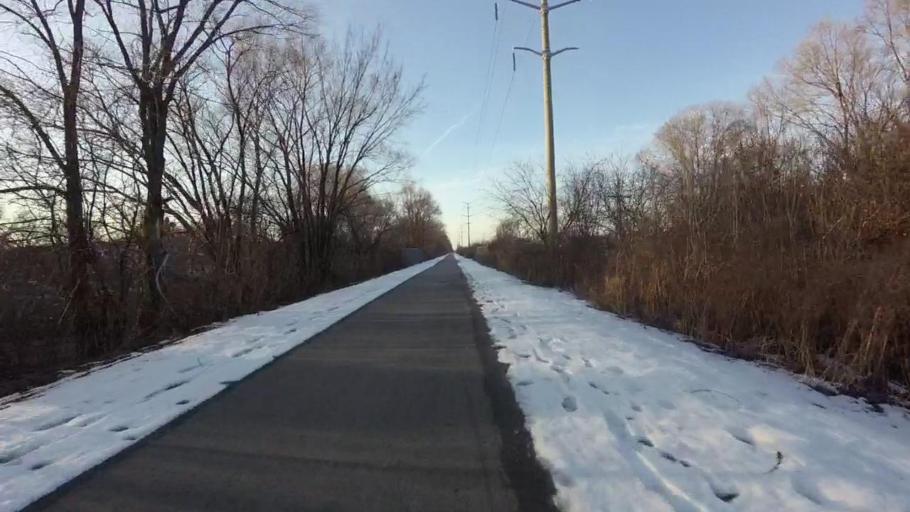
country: US
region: Wisconsin
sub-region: Milwaukee County
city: Glendale
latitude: 43.1208
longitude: -87.9342
